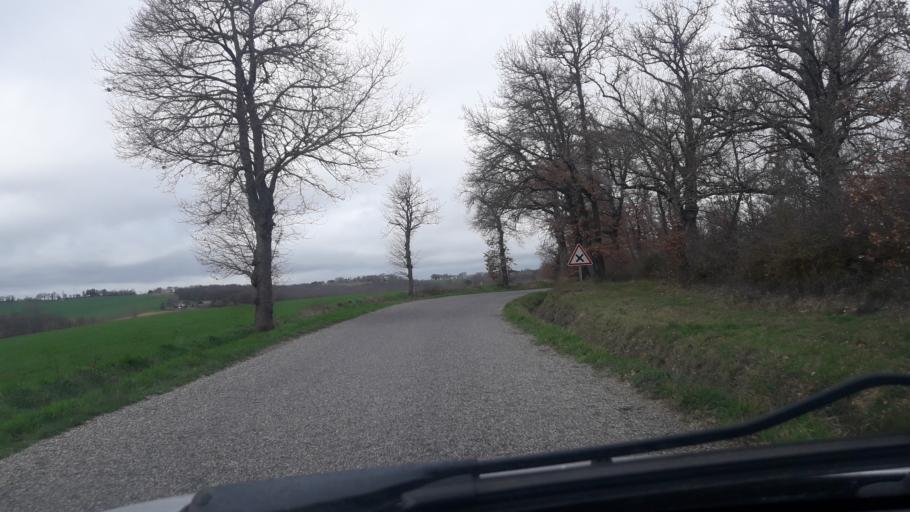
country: FR
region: Midi-Pyrenees
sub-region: Departement du Gers
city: Gimont
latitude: 43.6518
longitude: 0.9843
